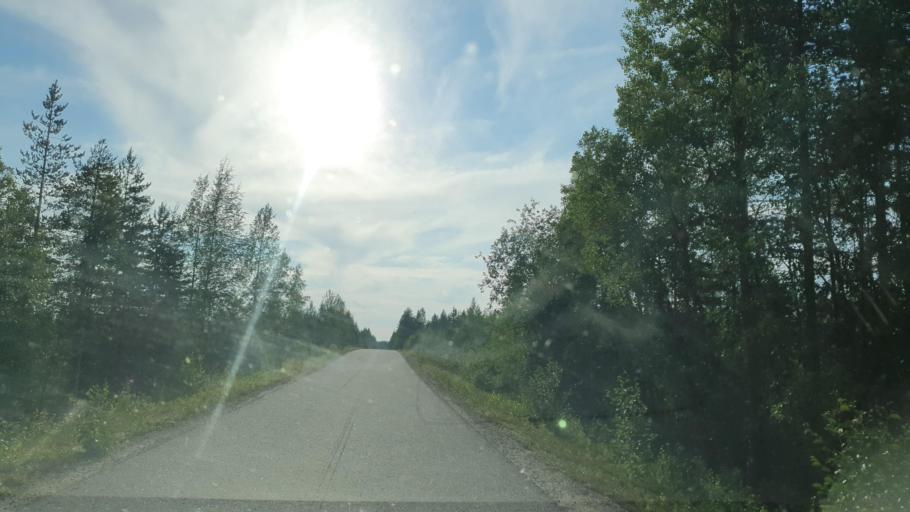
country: FI
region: Kainuu
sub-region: Kehys-Kainuu
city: Kuhmo
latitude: 64.2800
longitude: 29.4208
